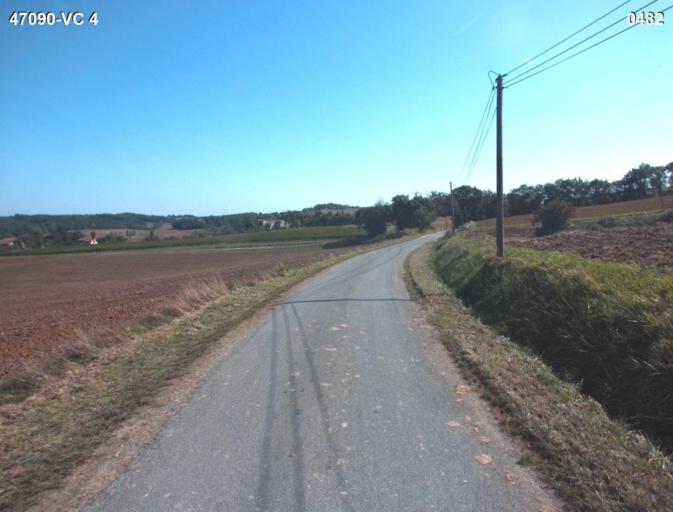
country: FR
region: Aquitaine
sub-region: Departement du Lot-et-Garonne
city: Vianne
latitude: 44.1773
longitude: 0.3491
